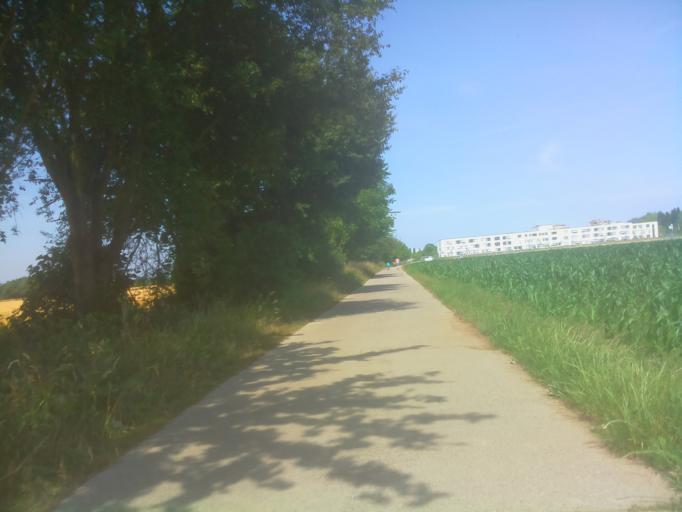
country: DE
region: Hesse
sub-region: Regierungsbezirk Darmstadt
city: Heppenheim an der Bergstrasse
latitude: 49.6238
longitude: 8.6295
